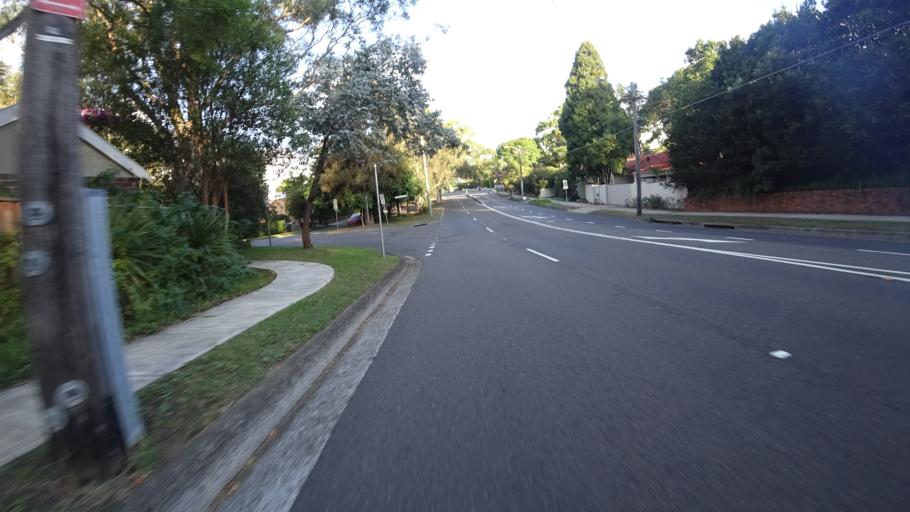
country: AU
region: New South Wales
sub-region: Lane Cove
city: Lane Cove
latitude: -33.8176
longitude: 151.1622
